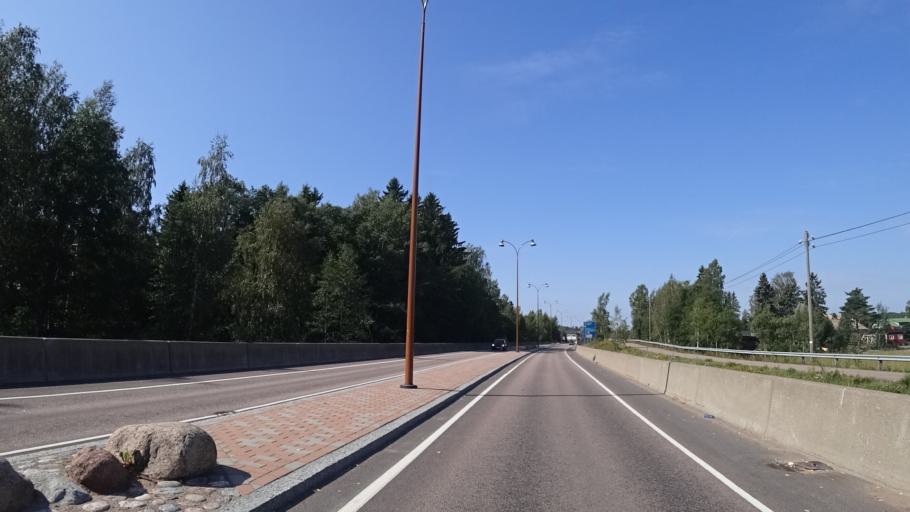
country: FI
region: Kymenlaakso
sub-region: Kotka-Hamina
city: Hamina
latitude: 60.5639
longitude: 27.1720
